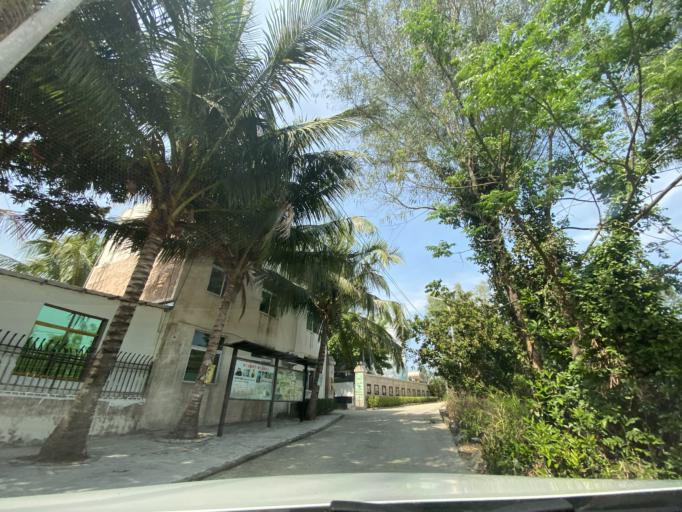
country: CN
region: Hainan
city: Yingzhou
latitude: 18.4103
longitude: 109.8325
